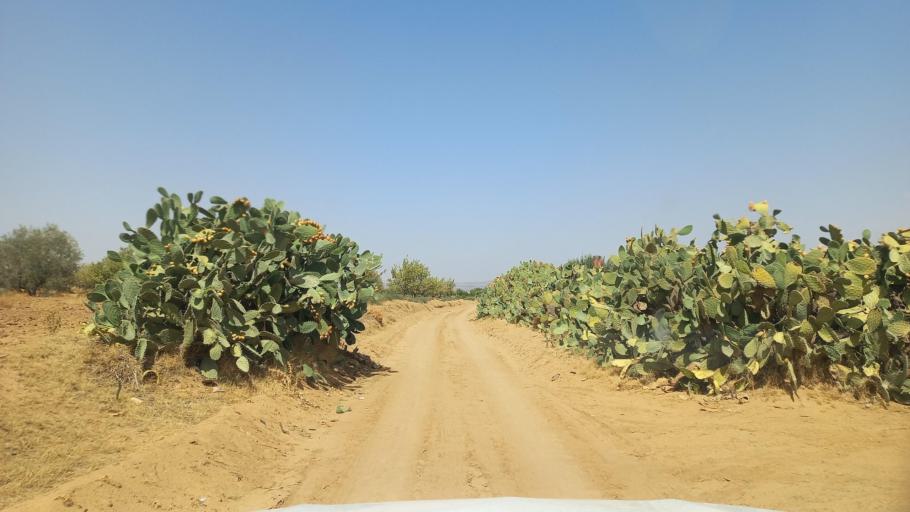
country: TN
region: Al Qasrayn
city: Kasserine
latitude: 35.2439
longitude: 9.0453
